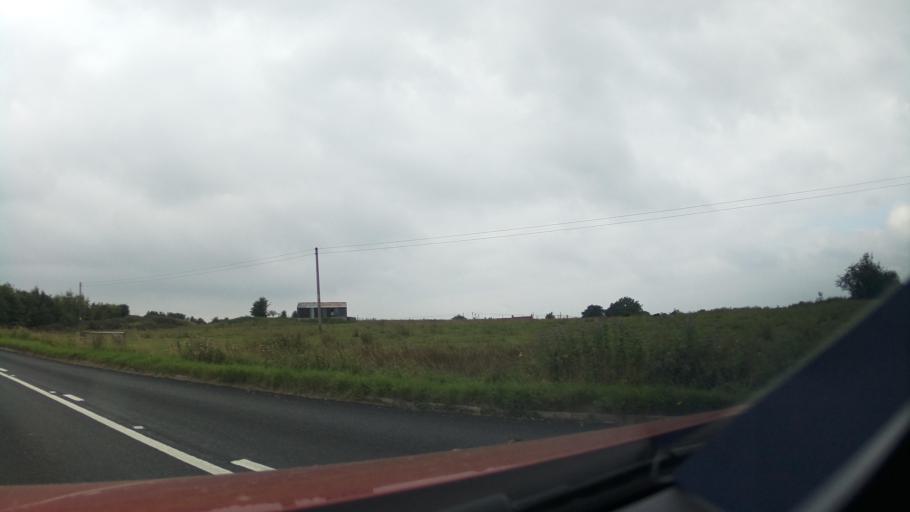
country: GB
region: England
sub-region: Staffordshire
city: Cheadle
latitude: 53.0317
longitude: -1.9059
